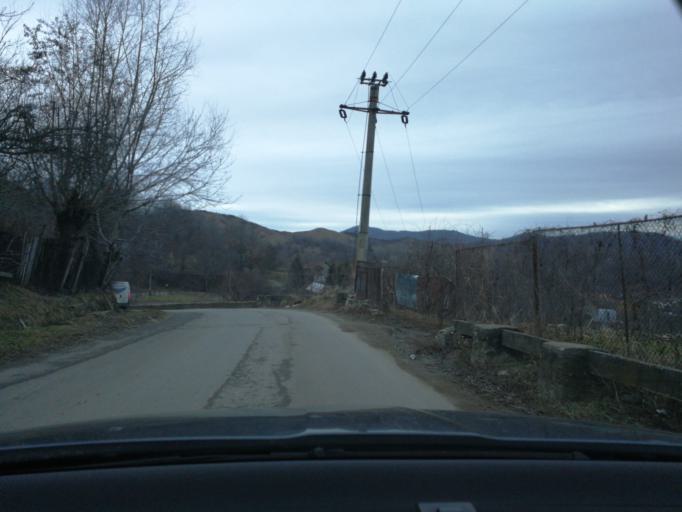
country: RO
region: Prahova
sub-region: Oras Breaza
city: Breaza
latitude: 45.1807
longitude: 25.6520
